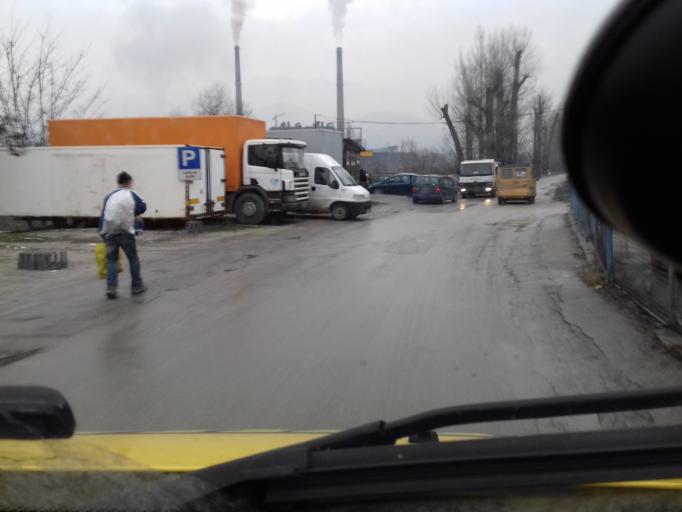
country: BA
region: Federation of Bosnia and Herzegovina
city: Zenica
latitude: 44.2192
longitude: 17.9101
